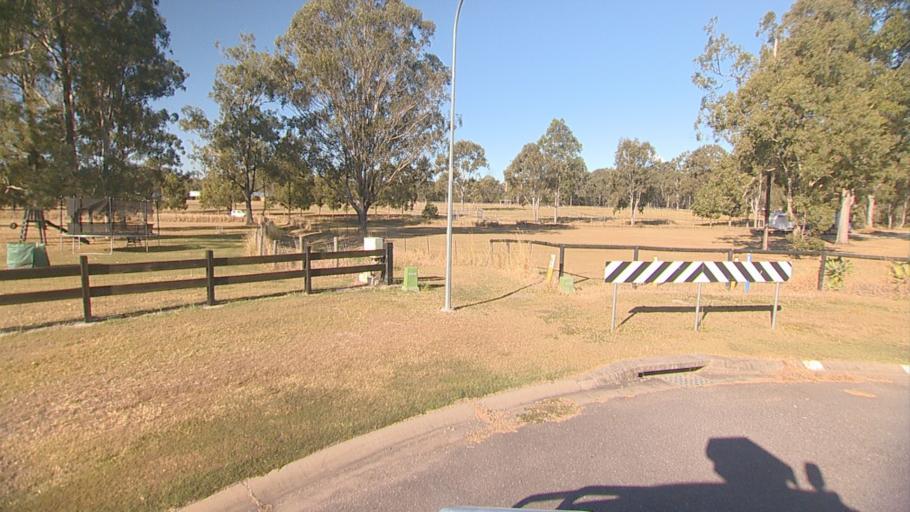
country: AU
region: Queensland
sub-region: Logan
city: North Maclean
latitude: -27.7868
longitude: 153.0268
